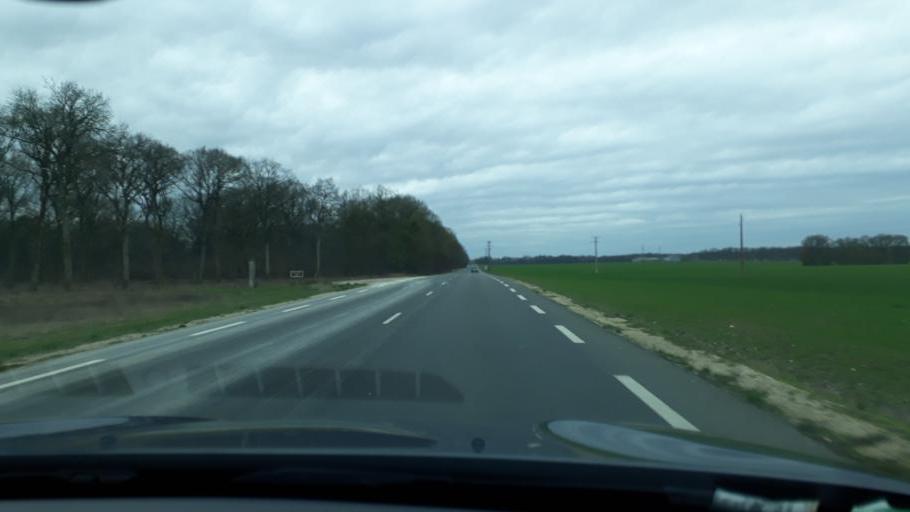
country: FR
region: Centre
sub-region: Departement du Loiret
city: Chanteau
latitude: 48.0249
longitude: 1.9690
